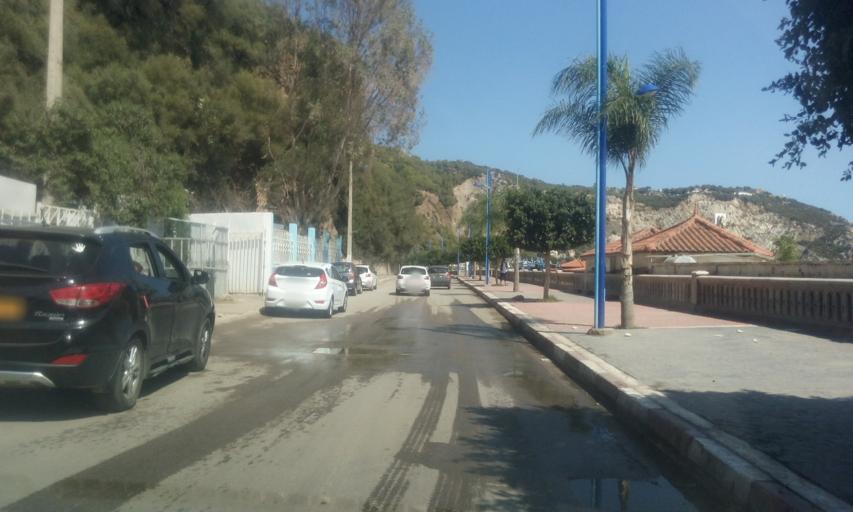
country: DZ
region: Bejaia
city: Bejaia
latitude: 36.7543
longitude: 5.0916
